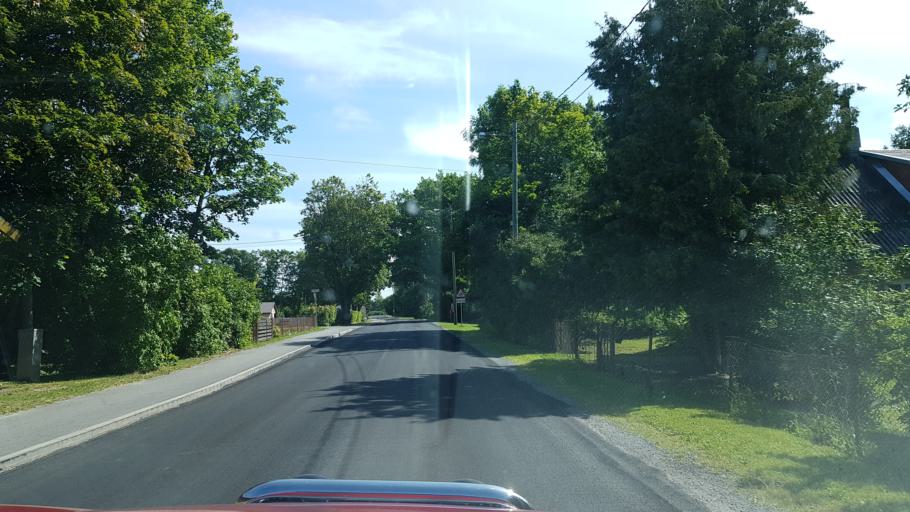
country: EE
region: Laeaene-Virumaa
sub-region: Tapa vald
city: Tapa
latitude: 59.1917
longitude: 25.8418
